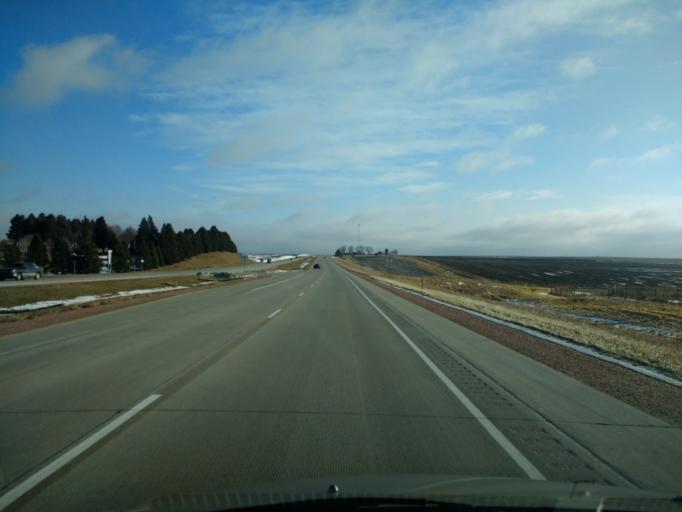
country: US
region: Iowa
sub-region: Ida County
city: Holstein
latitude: 42.4744
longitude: -95.5657
